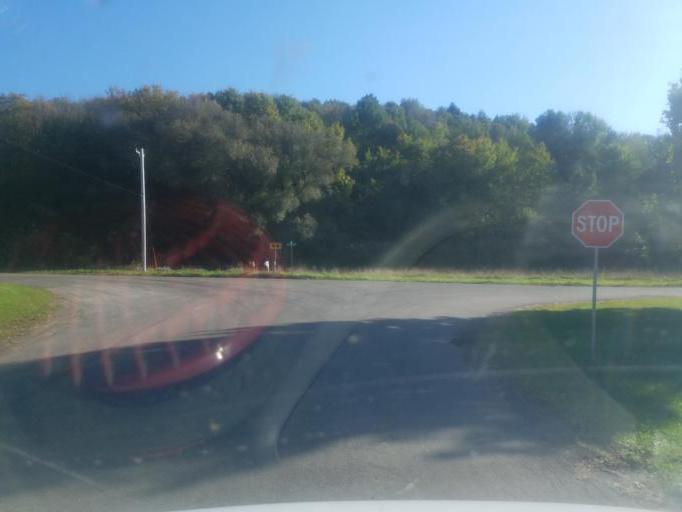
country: US
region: New York
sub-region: Allegany County
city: Cuba
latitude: 42.2465
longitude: -78.2548
